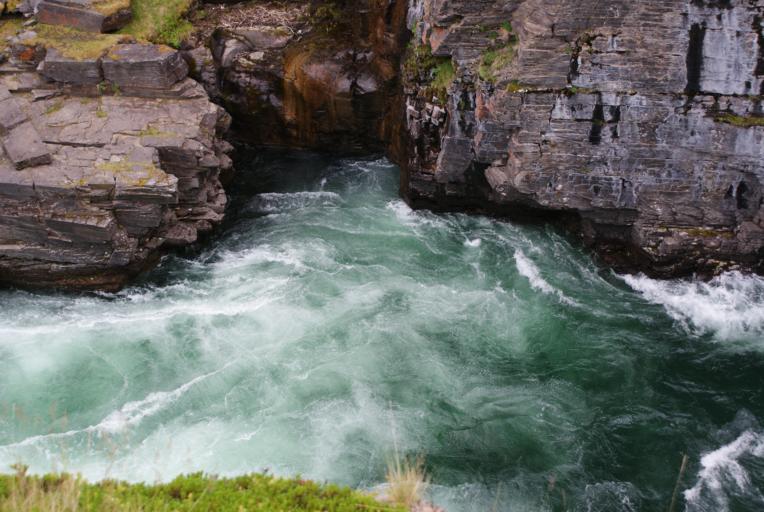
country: NO
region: Troms
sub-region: Bardu
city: Setermoen
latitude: 68.3600
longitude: 18.7757
